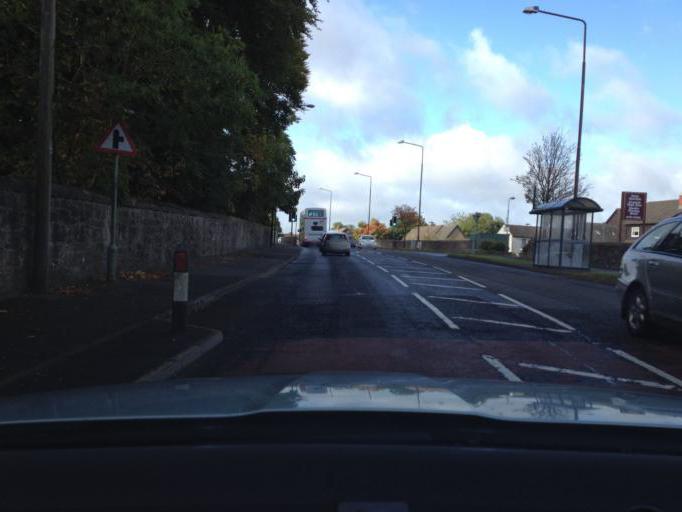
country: GB
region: Scotland
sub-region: West Lothian
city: West Calder
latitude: 55.8632
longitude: -3.5456
